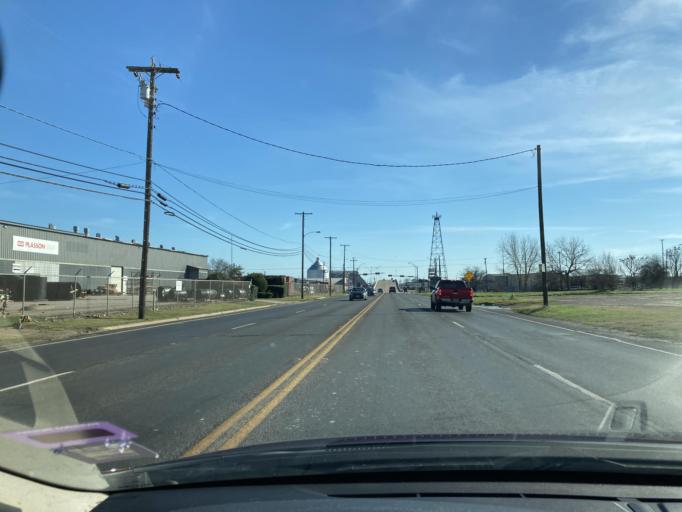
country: US
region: Texas
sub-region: Navarro County
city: Corsicana
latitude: 32.0976
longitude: -96.4618
